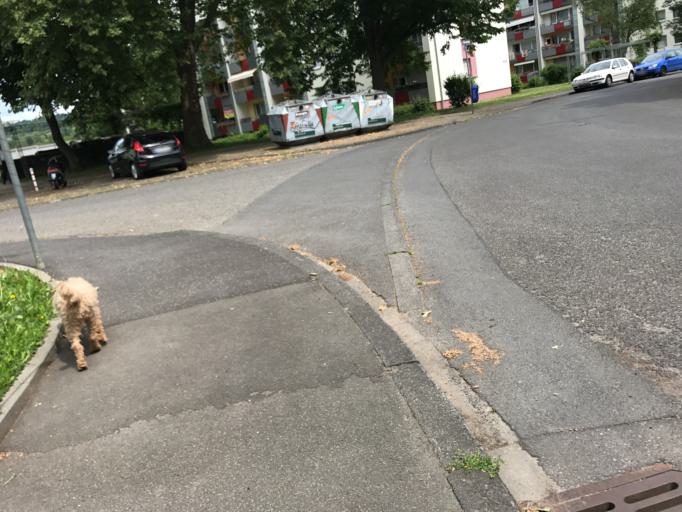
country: DE
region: Rheinland-Pfalz
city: Budenheim
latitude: 50.0466
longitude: 8.1861
